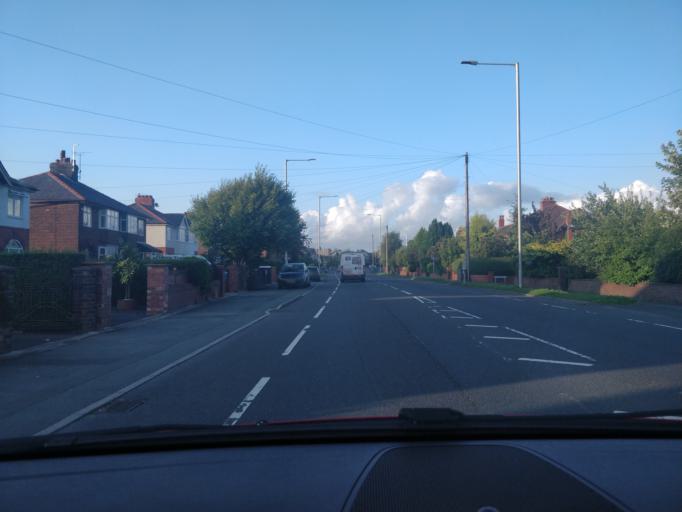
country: GB
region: England
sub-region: Lancashire
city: Preston
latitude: 53.7470
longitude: -2.7388
